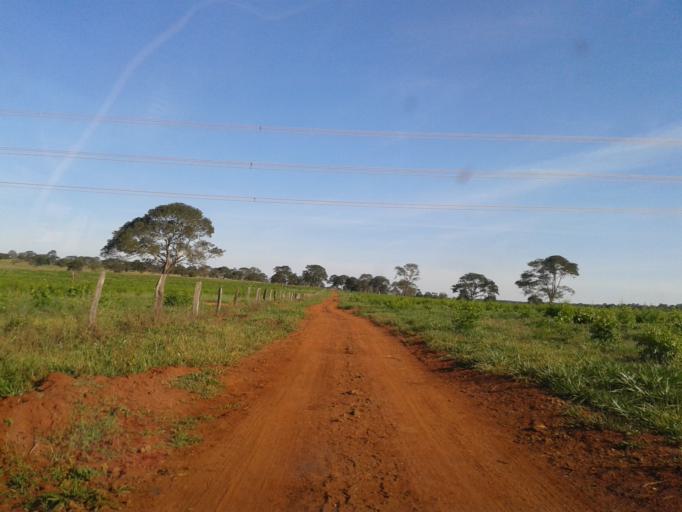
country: BR
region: Minas Gerais
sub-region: Santa Vitoria
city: Santa Vitoria
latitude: -19.0085
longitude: -50.3360
